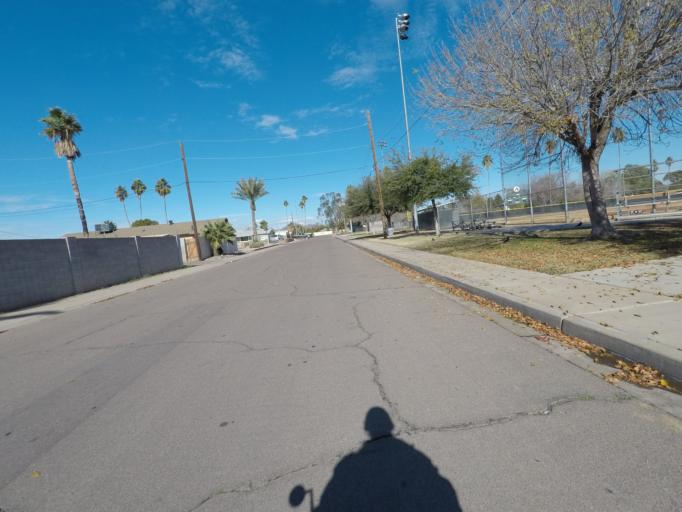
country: US
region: Arizona
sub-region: Maricopa County
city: Tempe Junction
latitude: 33.4085
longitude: -111.9500
